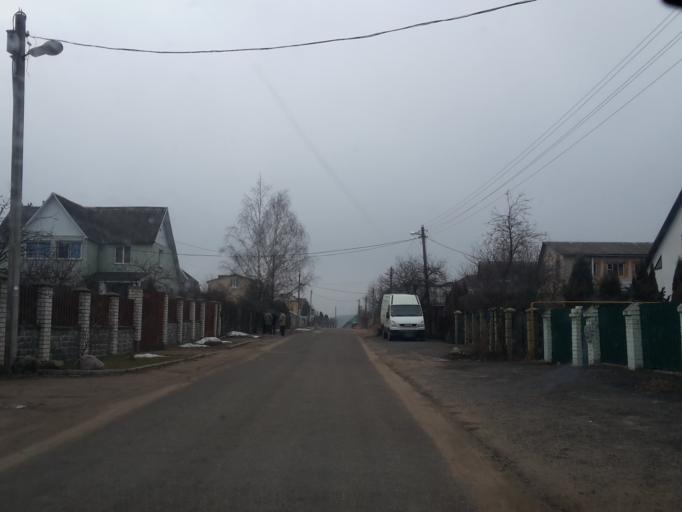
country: BY
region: Minsk
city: Zhdanovichy
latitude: 53.9185
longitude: 27.3950
